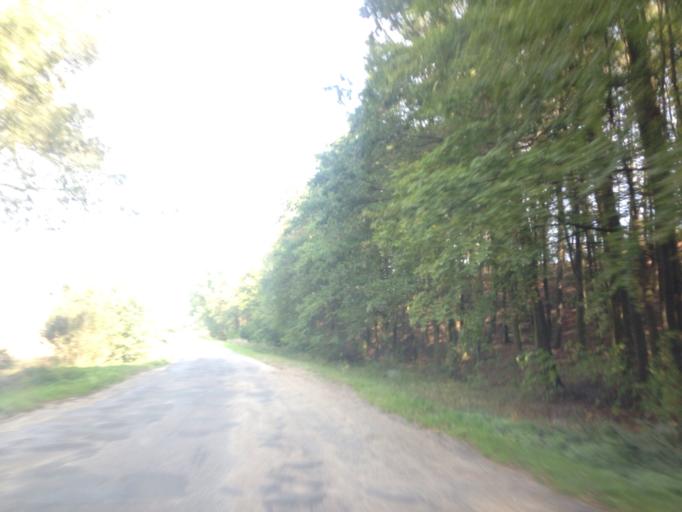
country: PL
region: Kujawsko-Pomorskie
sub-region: Powiat golubsko-dobrzynski
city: Golub-Dobrzyn
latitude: 53.1139
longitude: 19.0396
